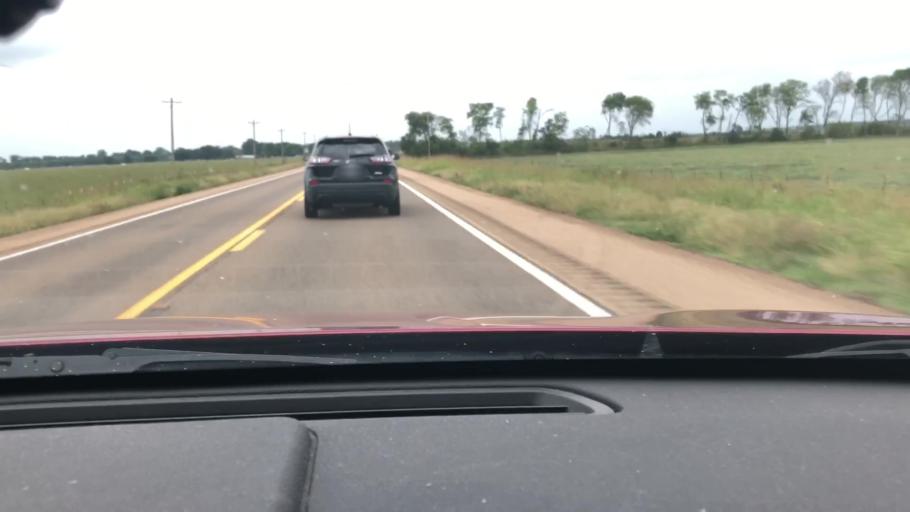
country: US
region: Arkansas
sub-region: Lafayette County
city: Lewisville
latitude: 33.3836
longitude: -93.7361
